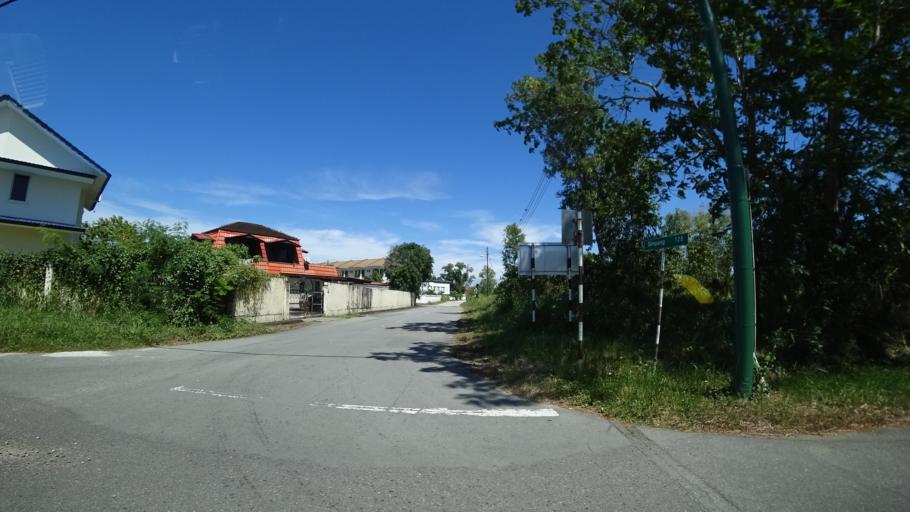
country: BN
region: Brunei and Muara
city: Bandar Seri Begawan
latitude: 4.9177
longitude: 114.9162
